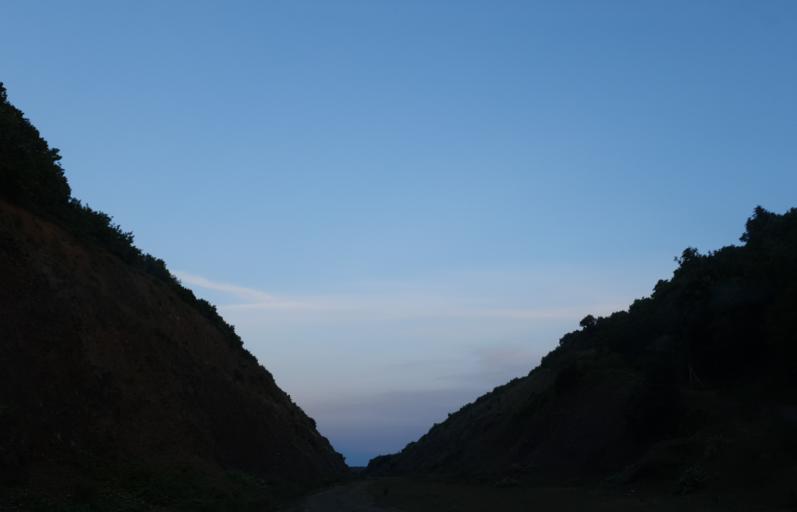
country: TR
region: Kirklareli
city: Salmydessus
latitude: 41.6872
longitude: 28.0819
